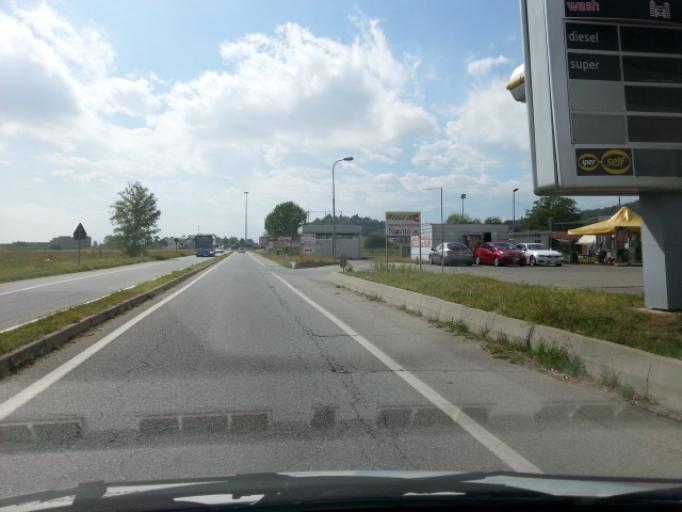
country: IT
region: Piedmont
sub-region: Provincia di Torino
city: Frossasco
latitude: 44.9090
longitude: 7.3613
